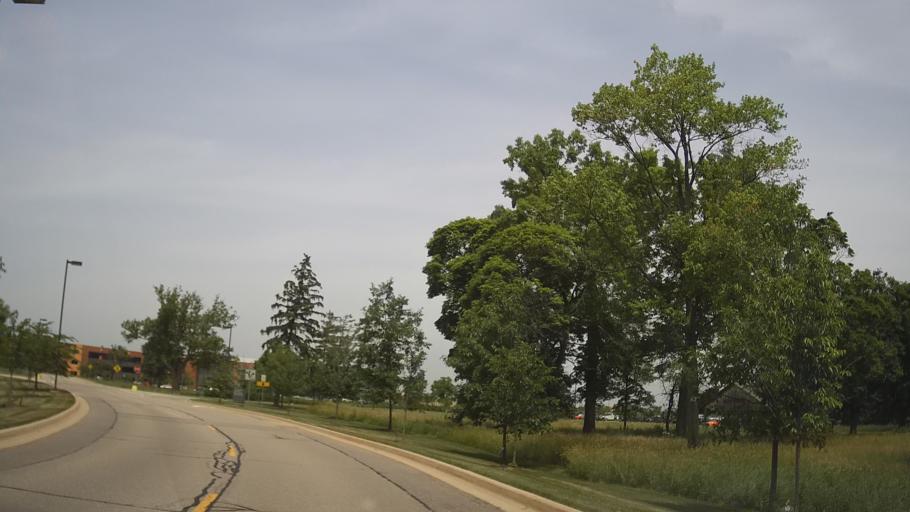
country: US
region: Michigan
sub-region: Washtenaw County
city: Milan
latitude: 42.1591
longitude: -83.6923
